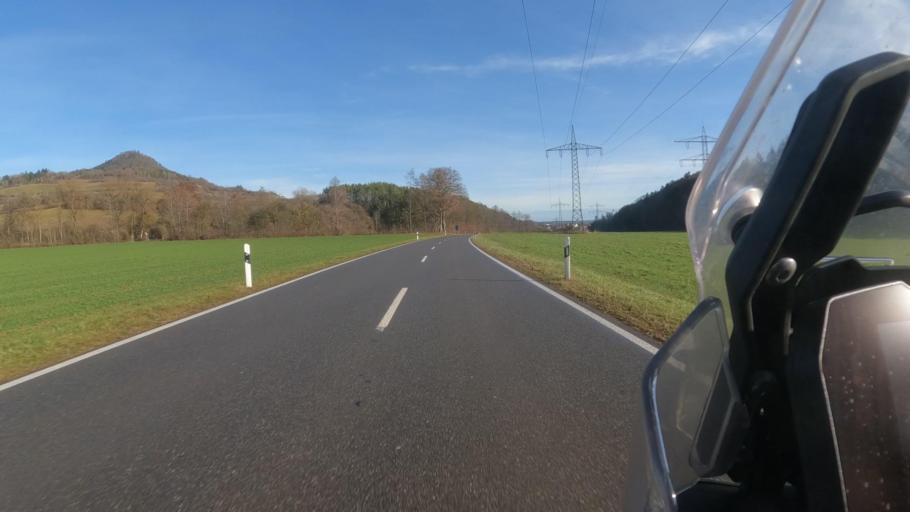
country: DE
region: Baden-Wuerttemberg
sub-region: Freiburg Region
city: Neuhausen
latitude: 47.8194
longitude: 8.7384
